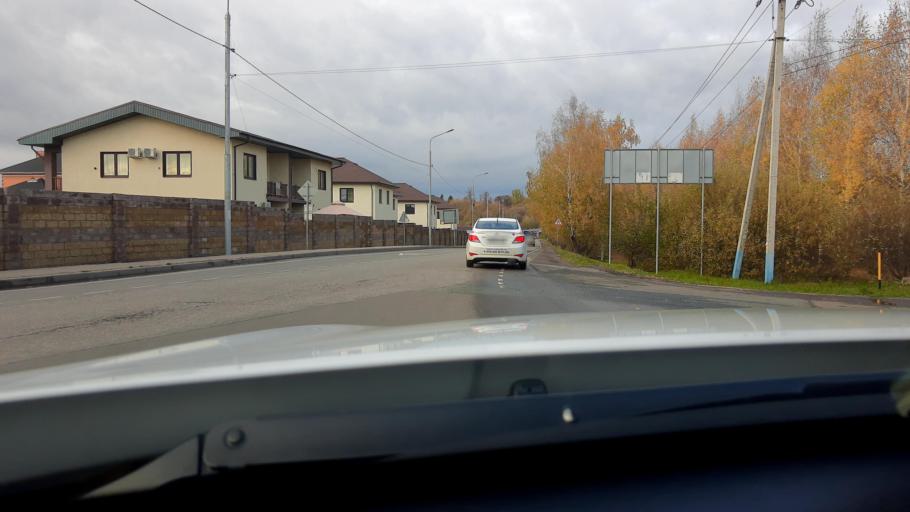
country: RU
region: Moskovskaya
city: Kokoshkino
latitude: 55.5311
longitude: 37.1535
